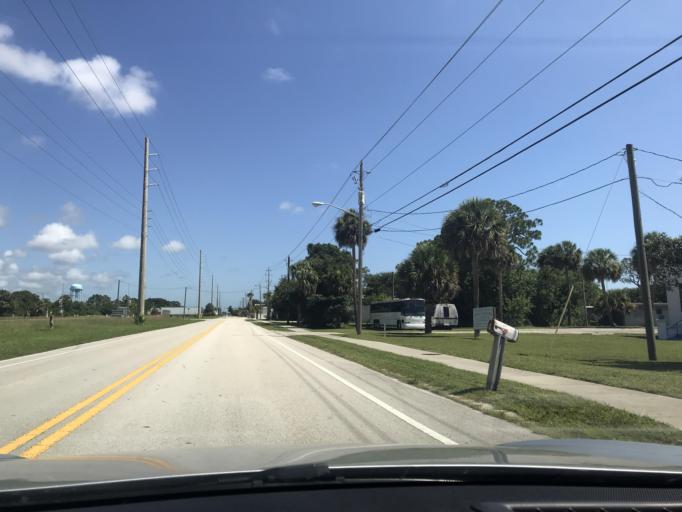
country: US
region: Florida
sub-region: Indian River County
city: Gifford
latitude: 27.6710
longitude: -80.4079
